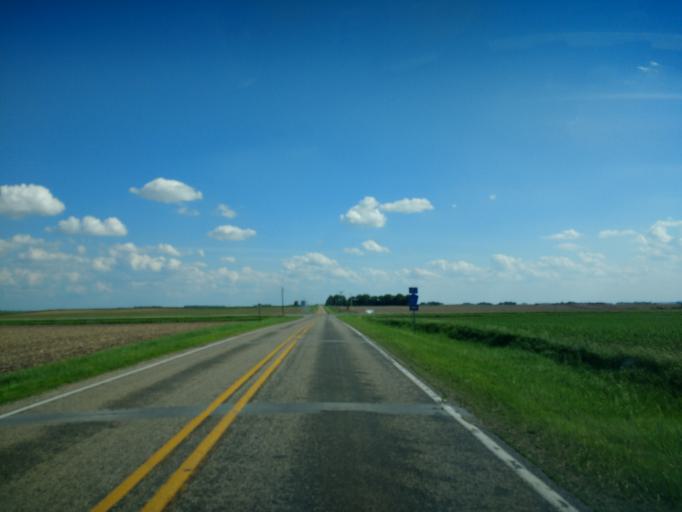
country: US
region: Iowa
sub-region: Dickinson County
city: Arnolds Park
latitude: 43.3298
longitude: -95.0725
